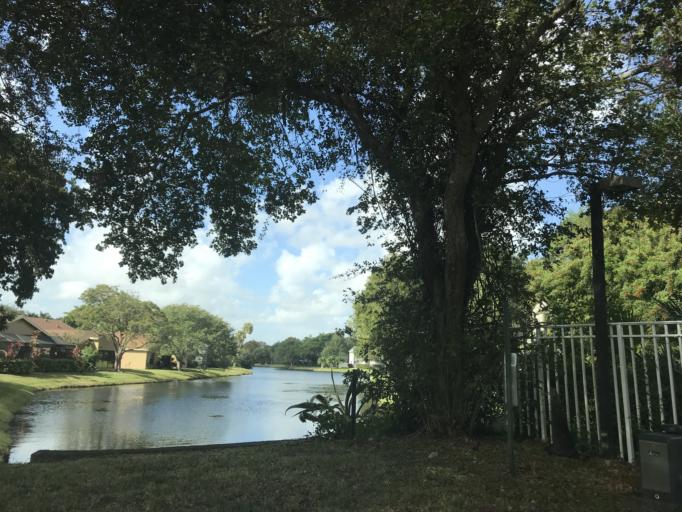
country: US
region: Florida
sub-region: Broward County
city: Coconut Creek
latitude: 26.2639
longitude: -80.1888
